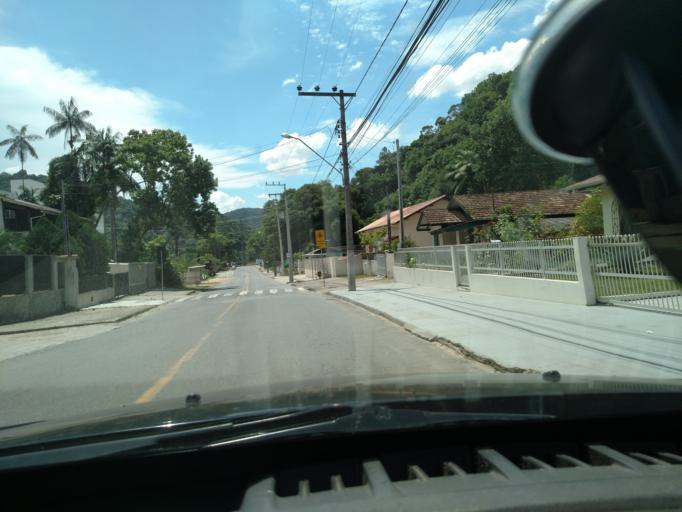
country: BR
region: Santa Catarina
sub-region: Blumenau
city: Blumenau
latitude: -26.9885
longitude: -49.0744
